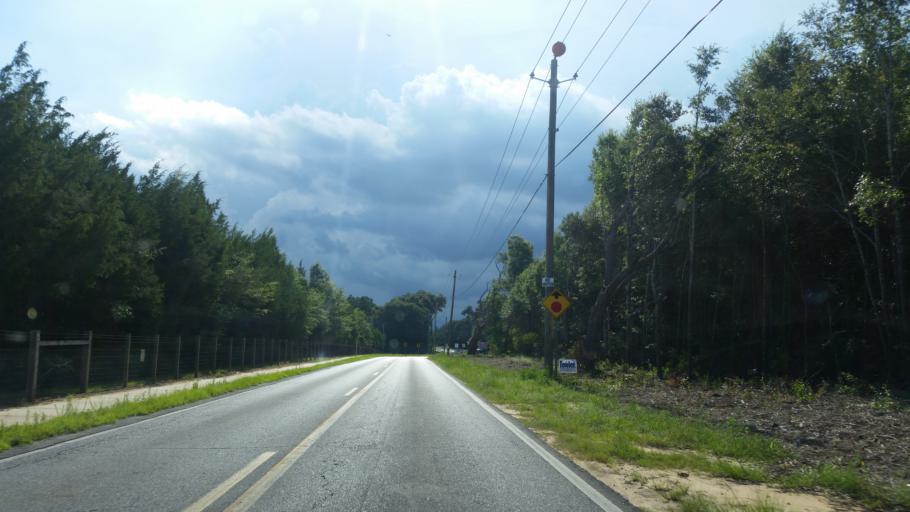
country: US
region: Florida
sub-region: Santa Rosa County
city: Pace
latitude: 30.6326
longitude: -87.1455
